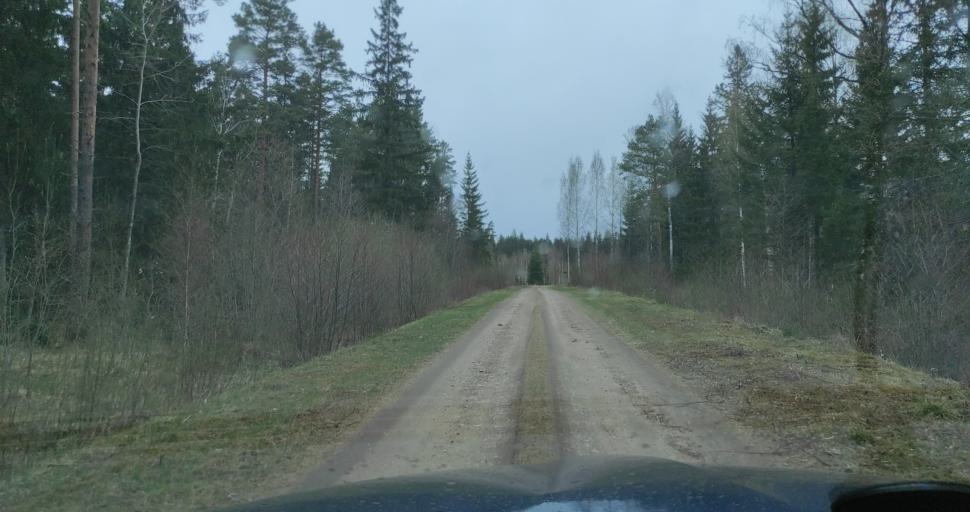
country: LV
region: Dundaga
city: Dundaga
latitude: 57.3607
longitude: 22.1513
